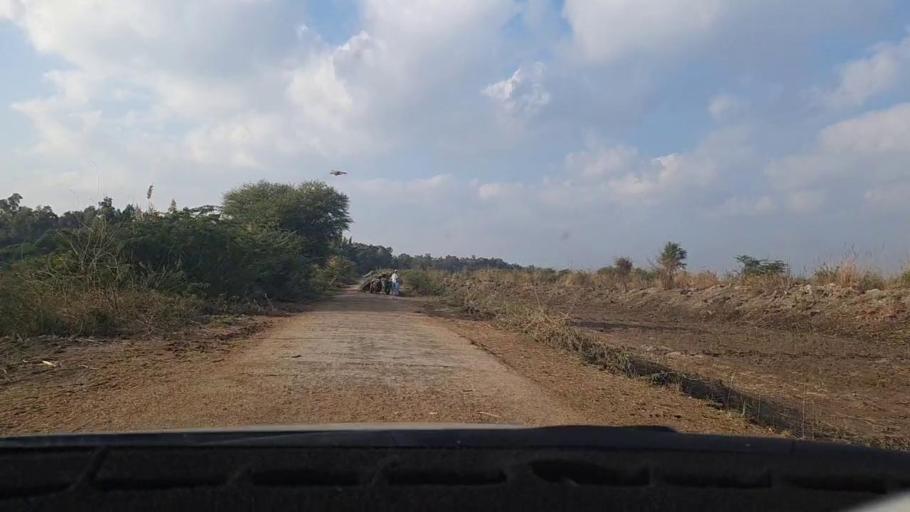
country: PK
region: Sindh
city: Tando Mittha Khan
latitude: 25.9100
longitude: 69.3054
